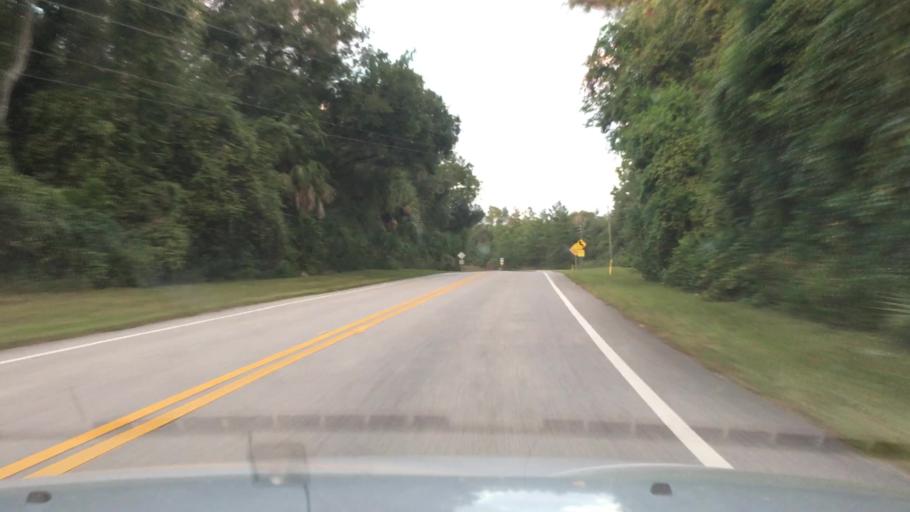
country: US
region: Florida
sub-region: Volusia County
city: Ormond Beach
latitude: 29.3030
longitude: -81.1033
